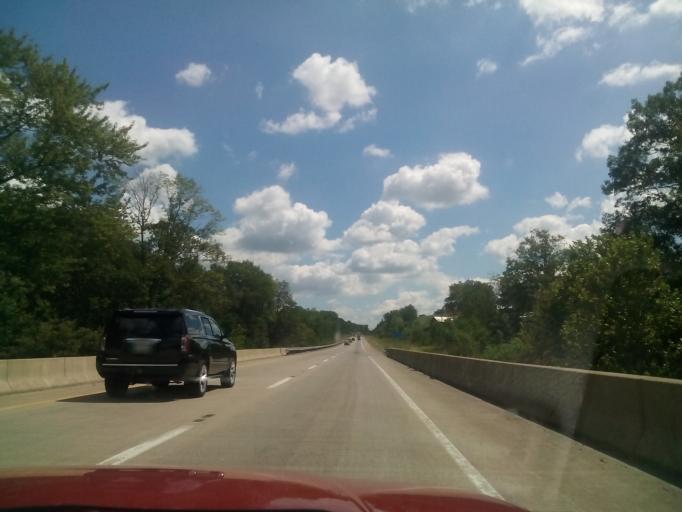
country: US
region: Pennsylvania
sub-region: Northumberland County
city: Milton
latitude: 41.0052
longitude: -76.7620
